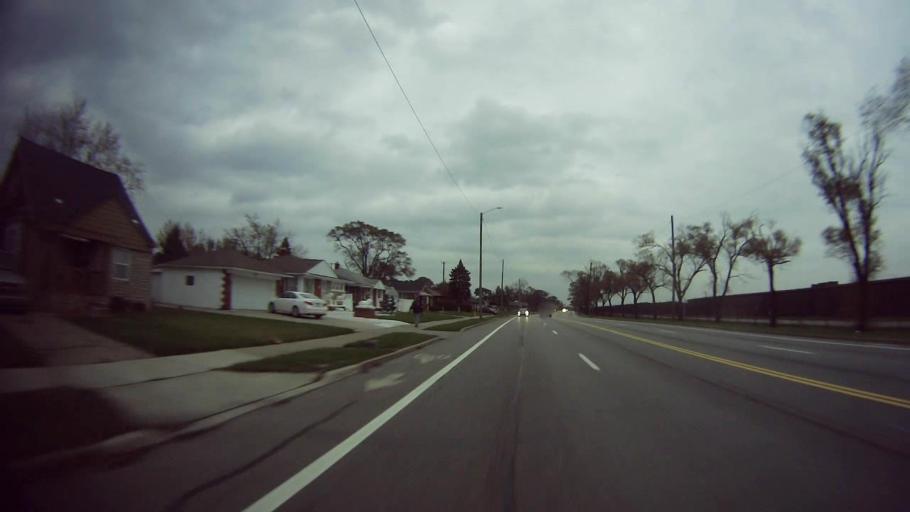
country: US
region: Michigan
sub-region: Wayne County
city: Hamtramck
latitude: 42.4180
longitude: -83.0120
